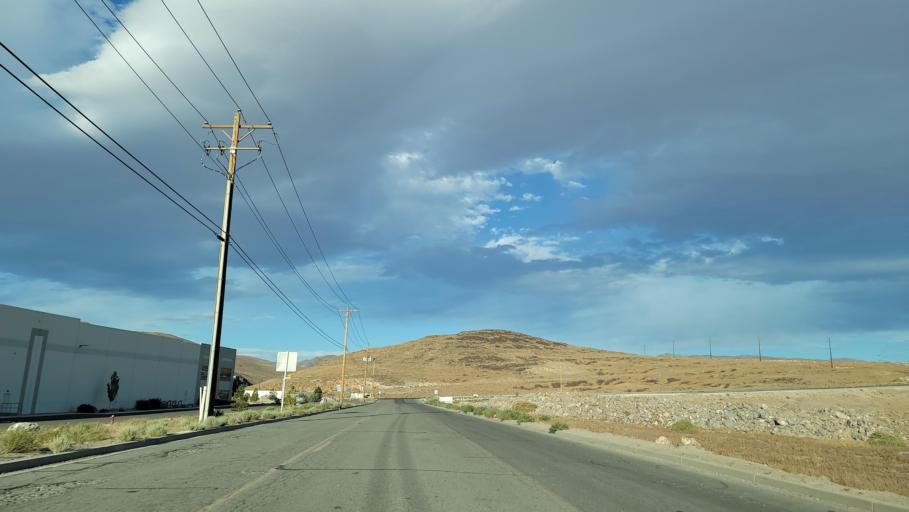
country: US
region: Nevada
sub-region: Lyon County
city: Stagecoach
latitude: 39.5529
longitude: -119.4937
